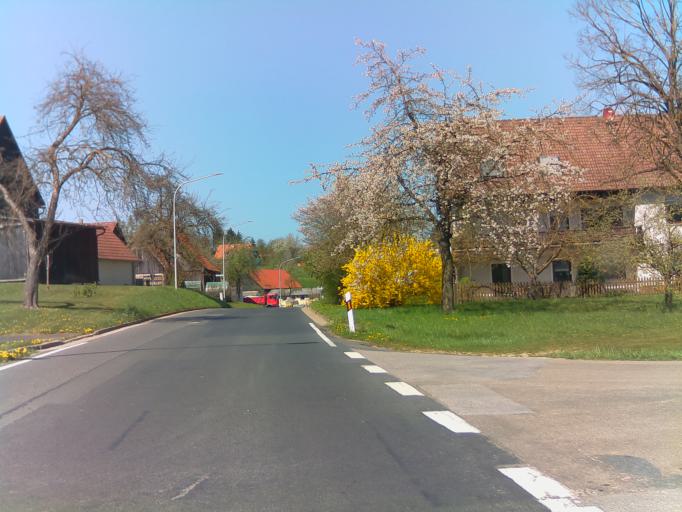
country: DE
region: Bavaria
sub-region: Upper Palatinate
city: Illschwang
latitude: 49.4348
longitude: 11.6183
